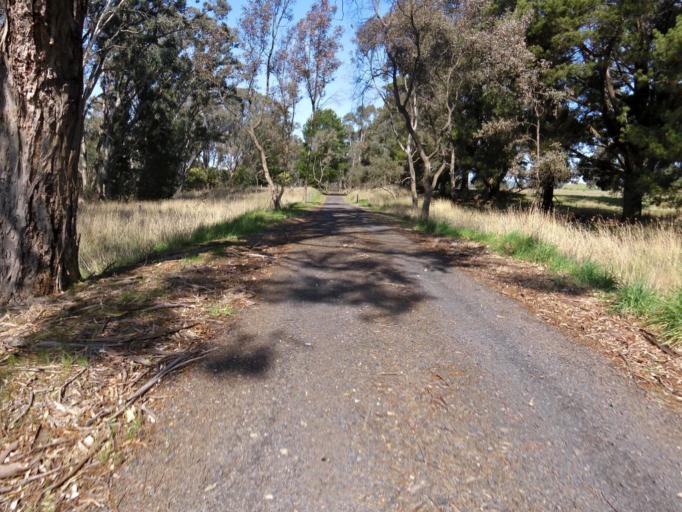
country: AU
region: Victoria
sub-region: Murrindindi
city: Alexandra
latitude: -36.9900
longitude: 145.7364
